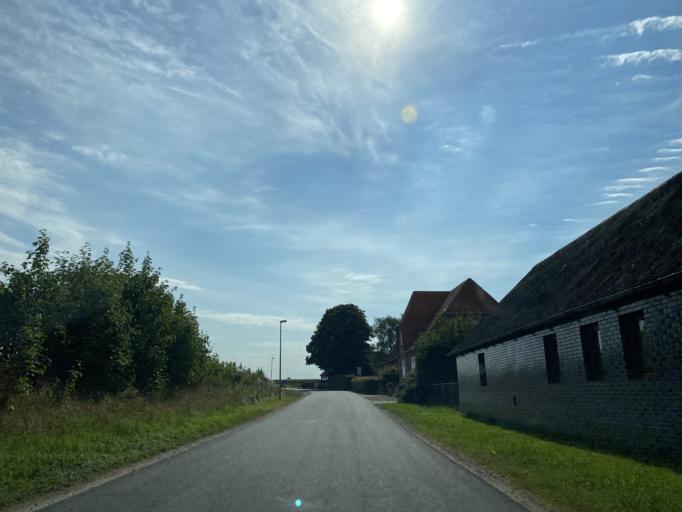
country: DK
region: Central Jutland
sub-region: Favrskov Kommune
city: Ulstrup
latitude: 56.3315
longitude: 9.7477
